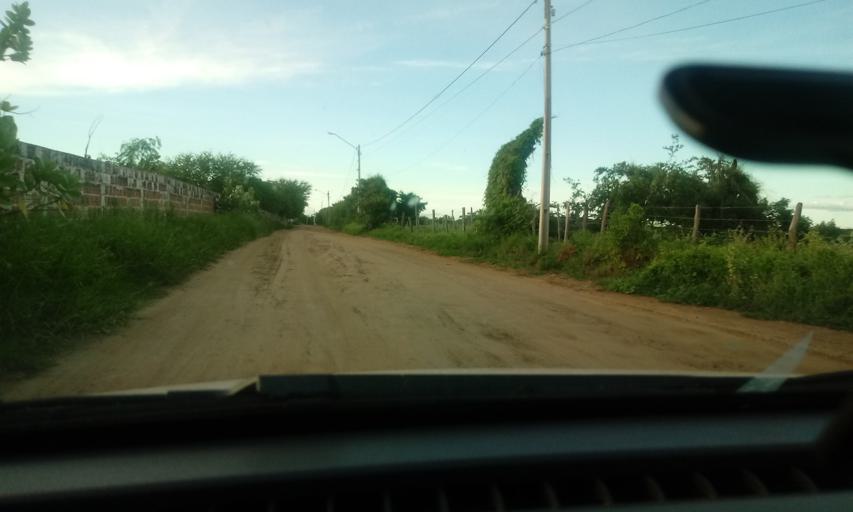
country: BR
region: Bahia
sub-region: Guanambi
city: Guanambi
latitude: -13.9145
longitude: -42.8457
